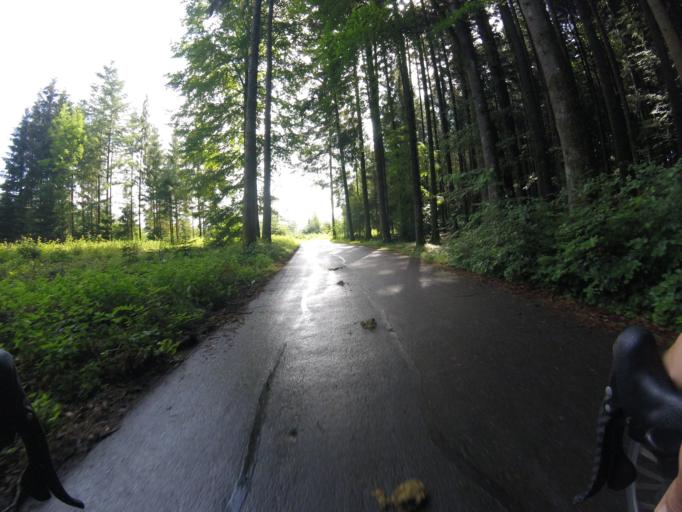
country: CH
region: Bern
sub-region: Bern-Mittelland District
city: Stettlen
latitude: 46.9405
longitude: 7.5282
